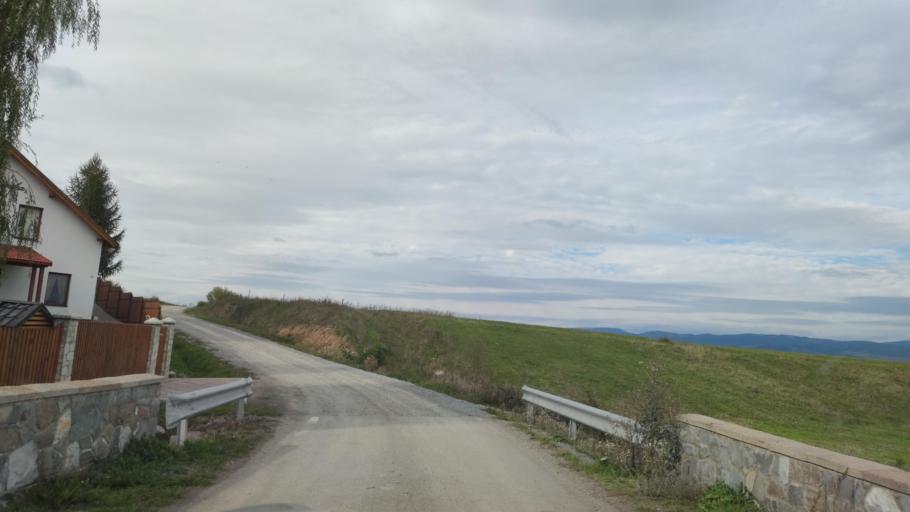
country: RO
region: Harghita
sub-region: Comuna Remetea
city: Remetea
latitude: 46.8132
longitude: 25.4229
